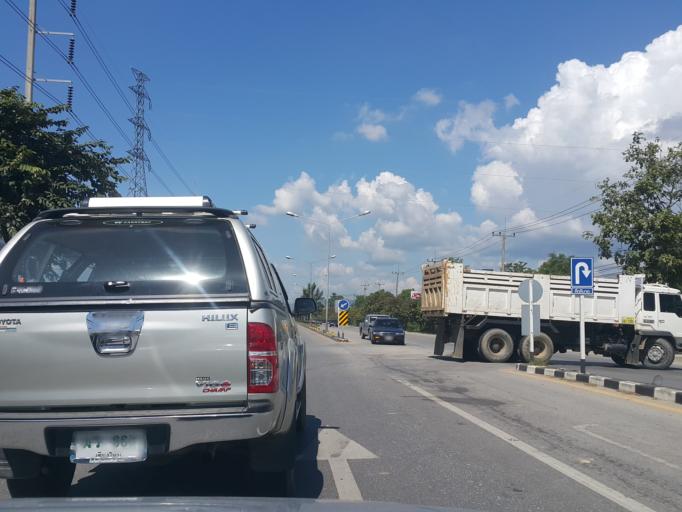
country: TH
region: Chiang Mai
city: San Sai
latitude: 18.8566
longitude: 99.0145
